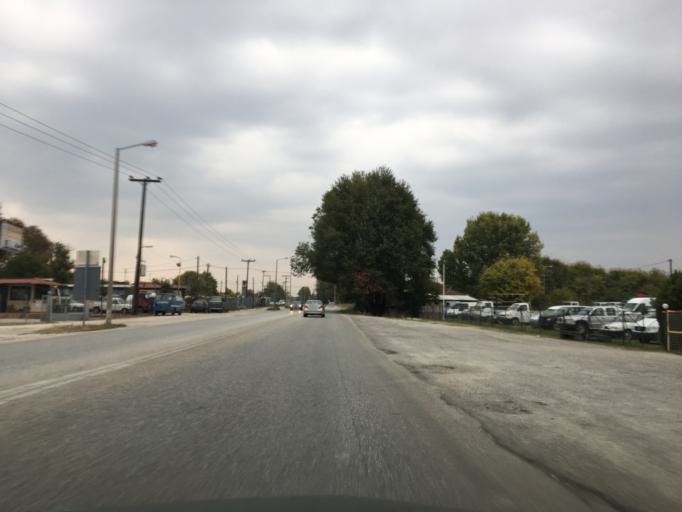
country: GR
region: Thessaly
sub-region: Trikala
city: Trikala
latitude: 39.5559
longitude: 21.7901
